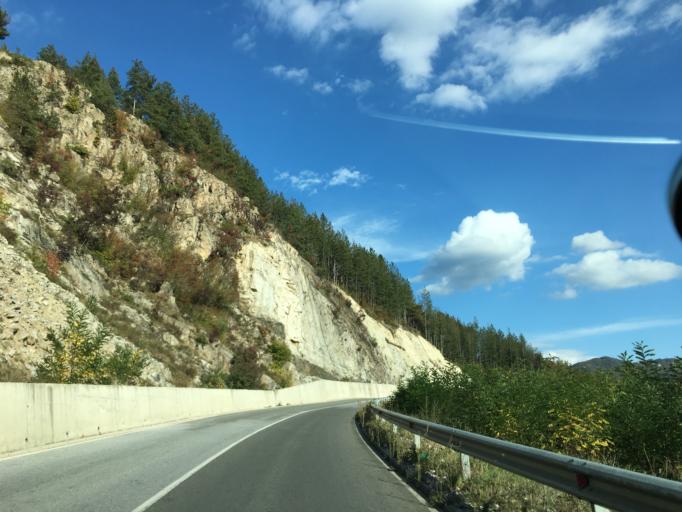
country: BG
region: Smolyan
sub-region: Obshtina Madan
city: Madan
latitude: 41.5354
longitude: 24.9143
